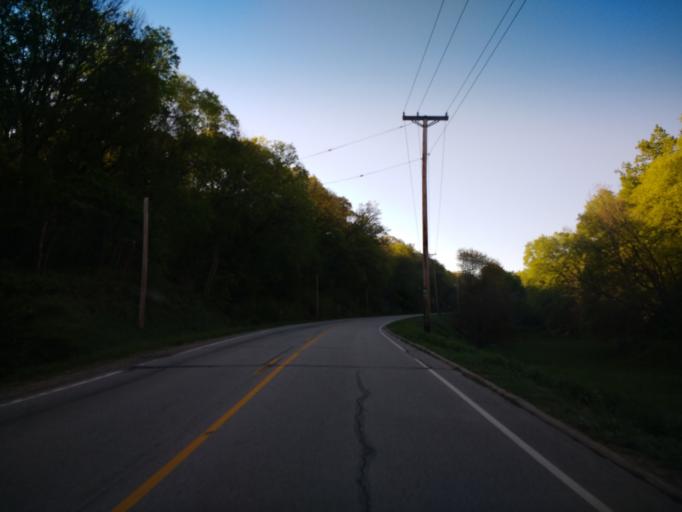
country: US
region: Iowa
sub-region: Harrison County
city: Missouri Valley
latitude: 41.4260
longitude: -95.8539
